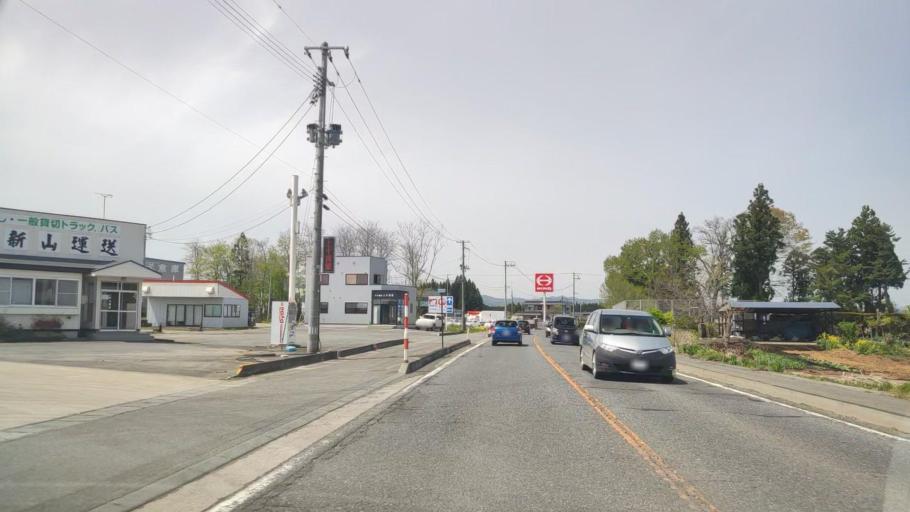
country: JP
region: Aomori
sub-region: Misawa Shi
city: Inuotose
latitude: 40.6738
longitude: 141.1786
